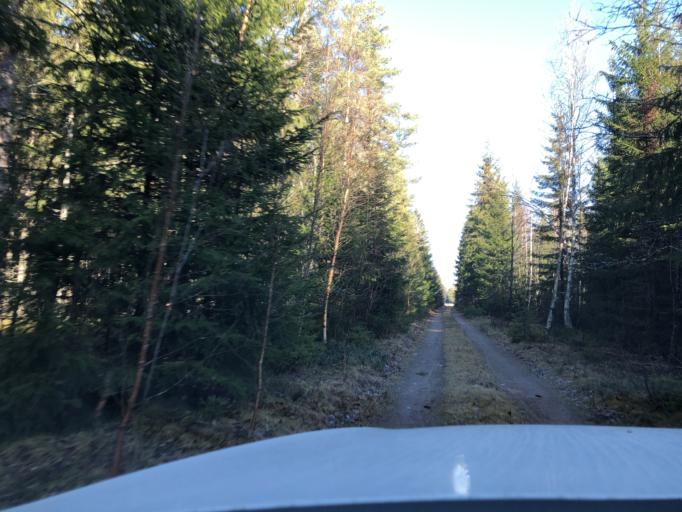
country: SE
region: Gaevleborg
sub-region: Gavle Kommun
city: Hedesunda
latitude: 60.3011
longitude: 16.9014
